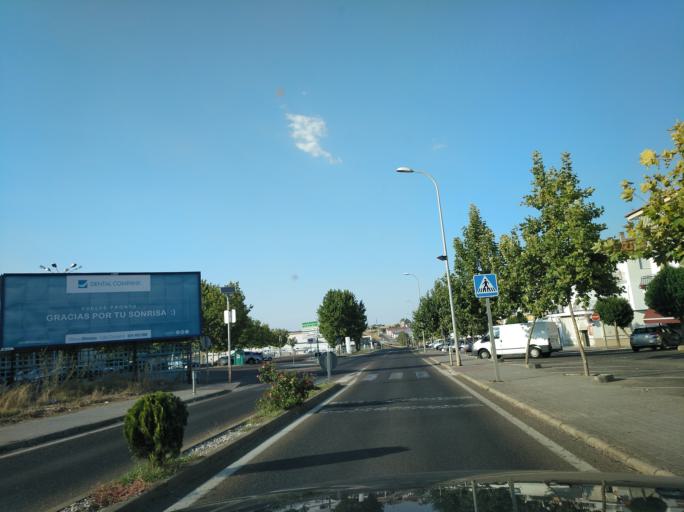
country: ES
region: Extremadura
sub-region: Provincia de Badajoz
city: Olivenza
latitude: 38.6901
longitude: -7.0934
